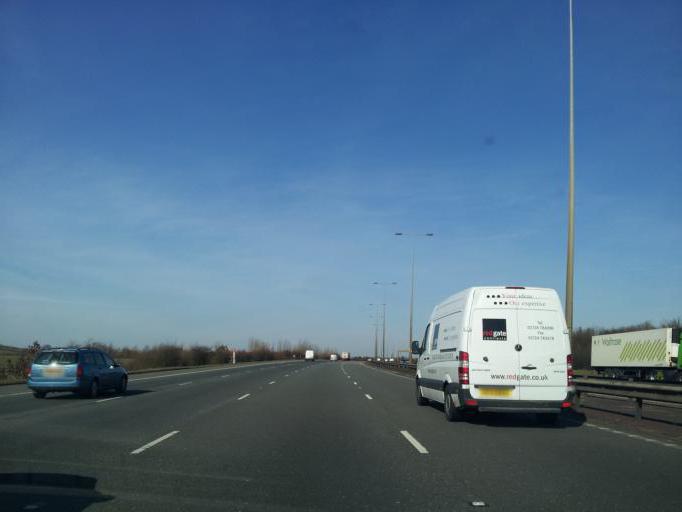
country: GB
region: England
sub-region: Cambridgeshire
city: Stilton
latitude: 52.4766
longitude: -0.2864
